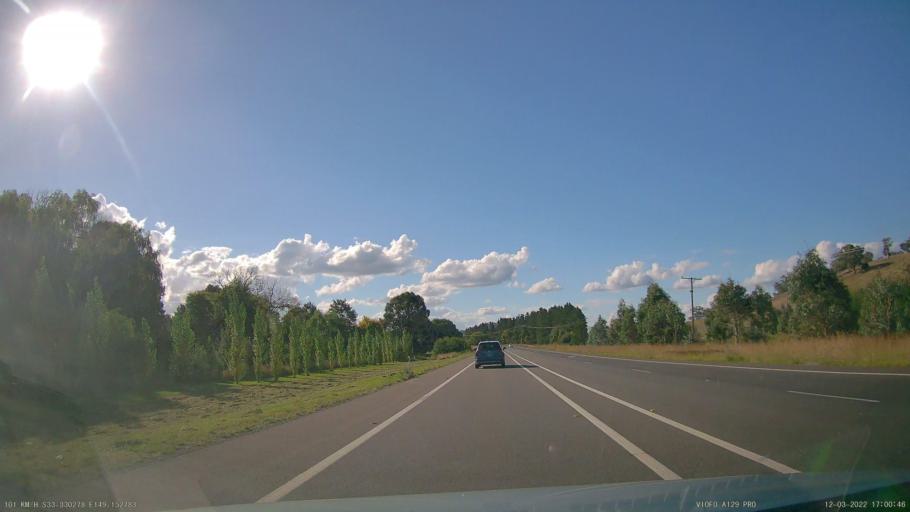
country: AU
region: New South Wales
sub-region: Orange Municipality
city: Orange
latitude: -33.3300
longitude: 149.1527
